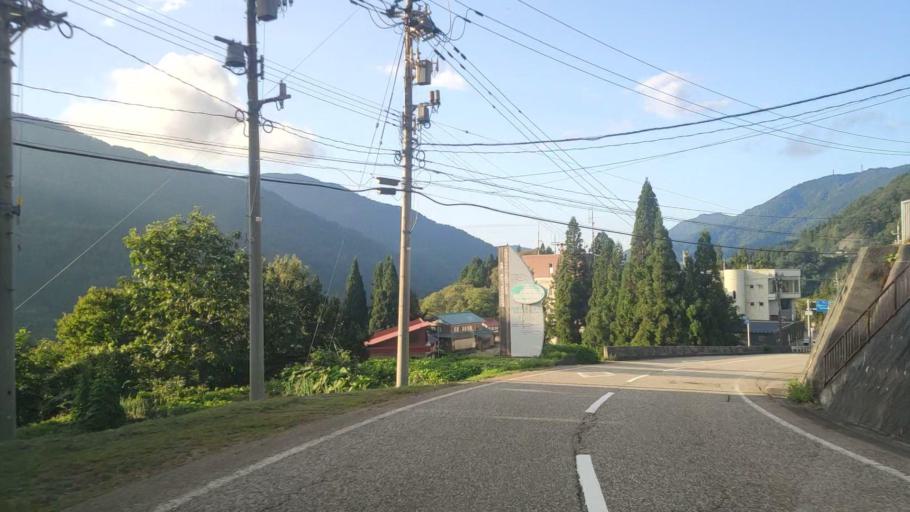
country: JP
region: Toyama
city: Yatsuomachi-higashikumisaka
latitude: 36.4562
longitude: 137.0264
